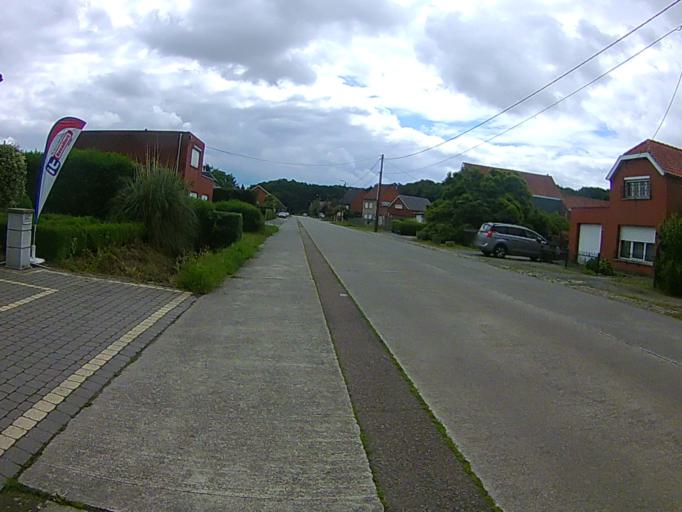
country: BE
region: Flanders
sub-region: Provincie Antwerpen
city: Heist-op-den-Berg
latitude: 51.1066
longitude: 4.7097
